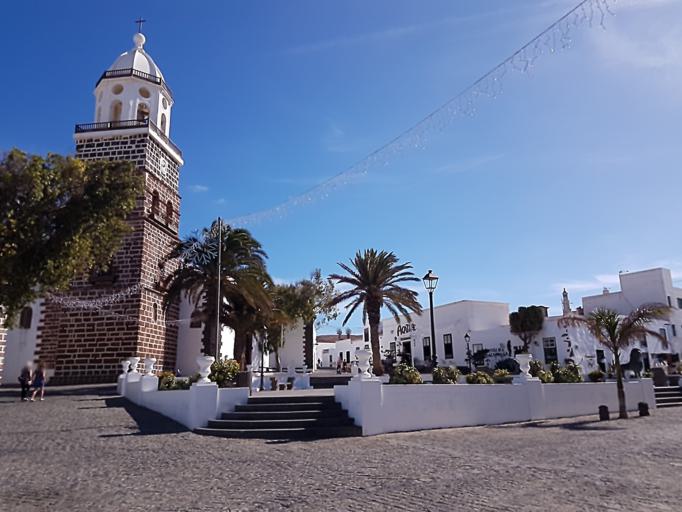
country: ES
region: Canary Islands
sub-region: Provincia de Las Palmas
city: Teguise
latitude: 29.0595
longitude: -13.5603
